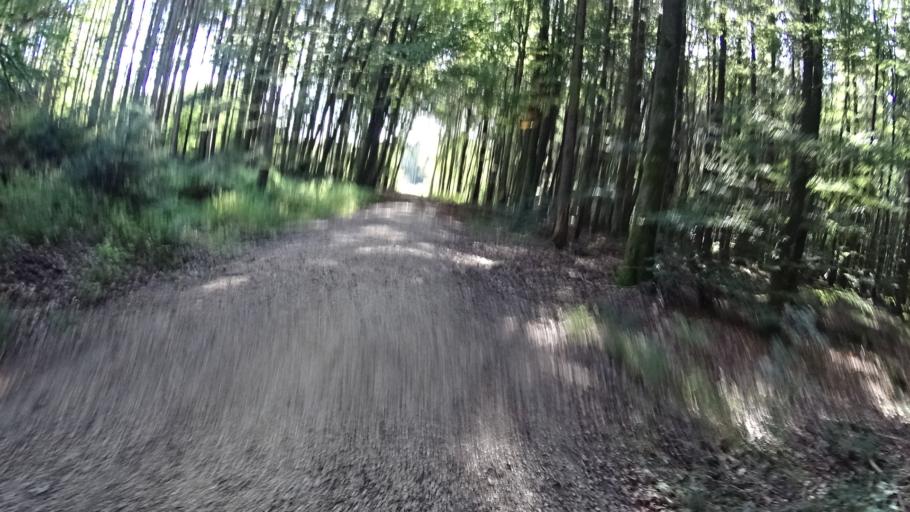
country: DE
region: Bavaria
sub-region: Upper Bavaria
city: Walting
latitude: 48.8875
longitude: 11.2821
